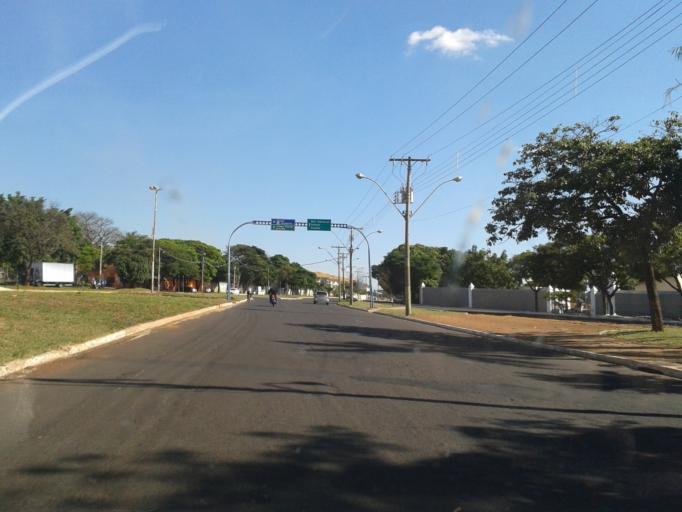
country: BR
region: Minas Gerais
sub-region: Uberaba
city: Uberaba
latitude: -19.7424
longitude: -47.9602
